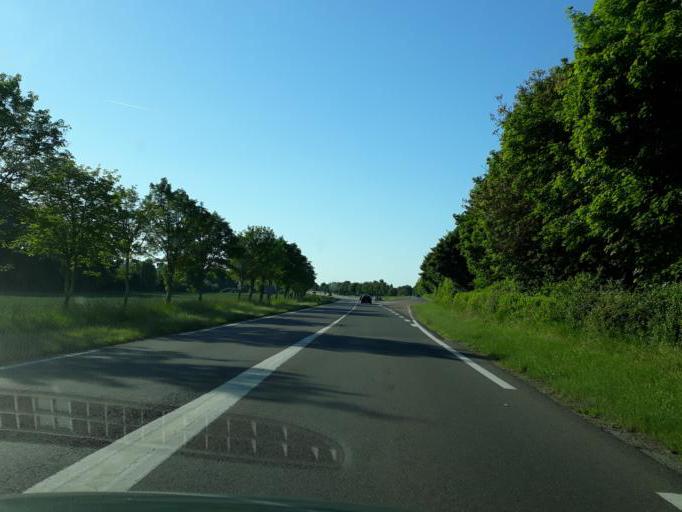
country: FR
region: Centre
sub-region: Departement du Loiret
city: Bonny-sur-Loire
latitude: 47.5429
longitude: 2.8570
